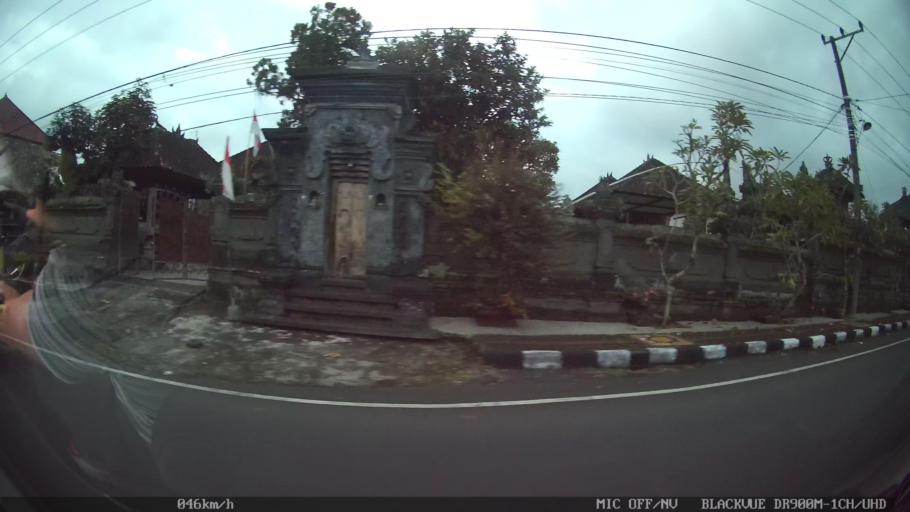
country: ID
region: Bali
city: Penebel
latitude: -8.4240
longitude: 115.1446
